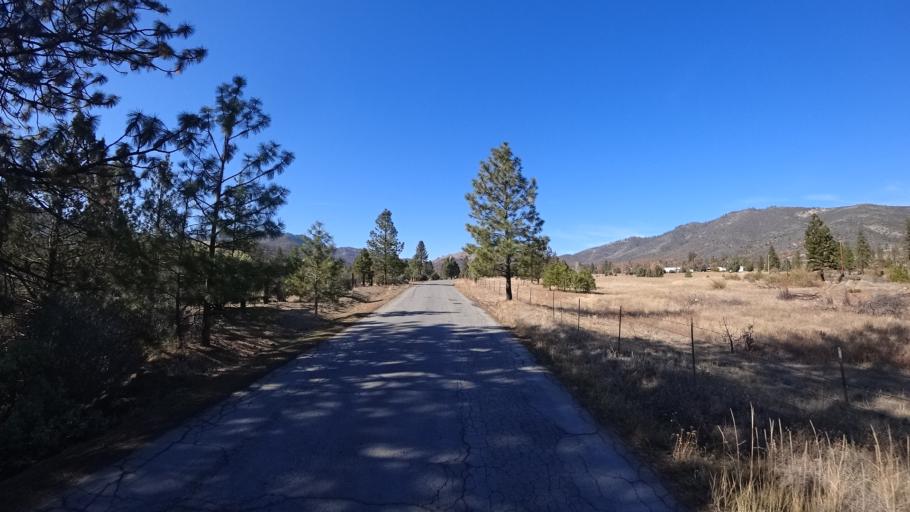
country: US
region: California
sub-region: Siskiyou County
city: Yreka
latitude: 41.7667
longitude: -122.6290
